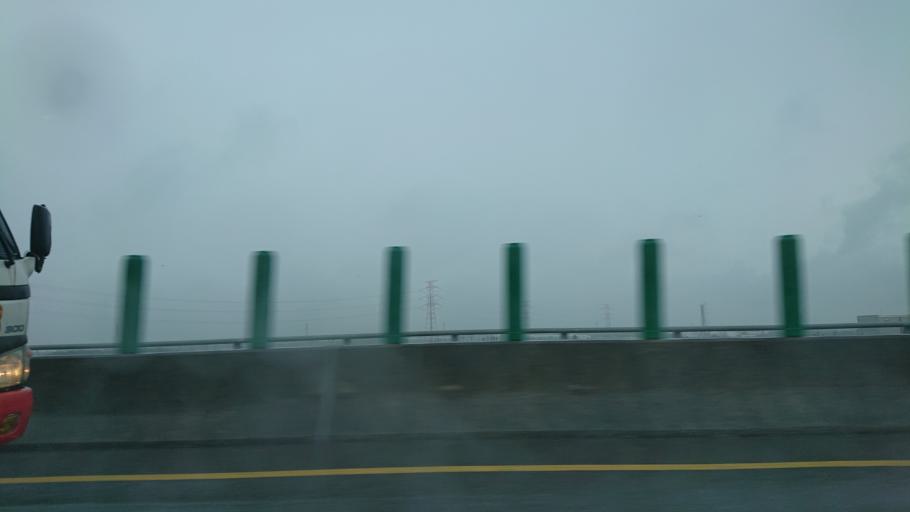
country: TW
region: Taiwan
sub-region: Yunlin
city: Douliu
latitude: 23.7711
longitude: 120.2719
